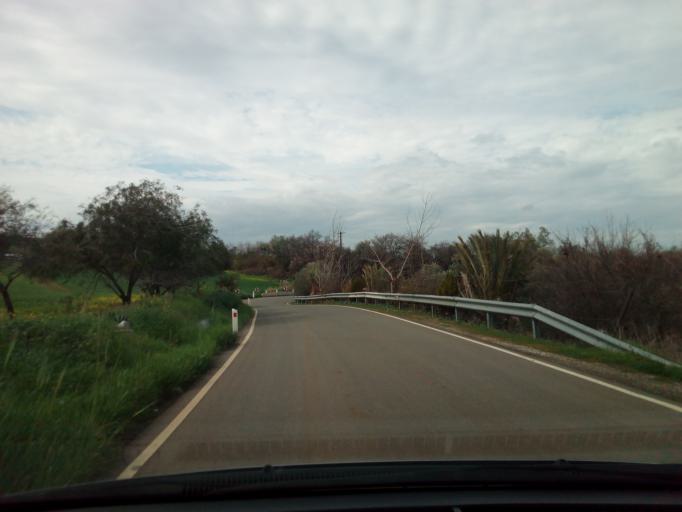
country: CY
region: Lefkosia
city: Astromeritis
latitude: 35.0967
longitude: 32.9865
